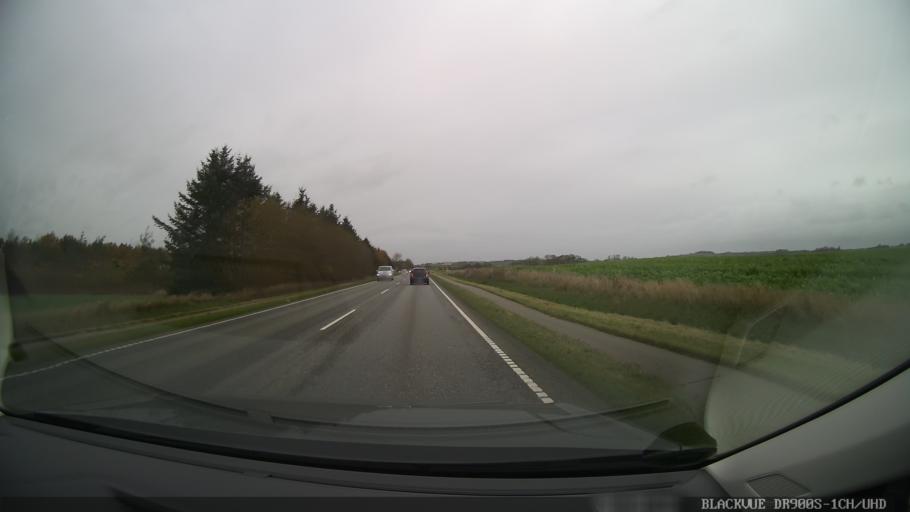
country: DK
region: North Denmark
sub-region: Thisted Kommune
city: Thisted
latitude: 56.8439
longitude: 8.7027
